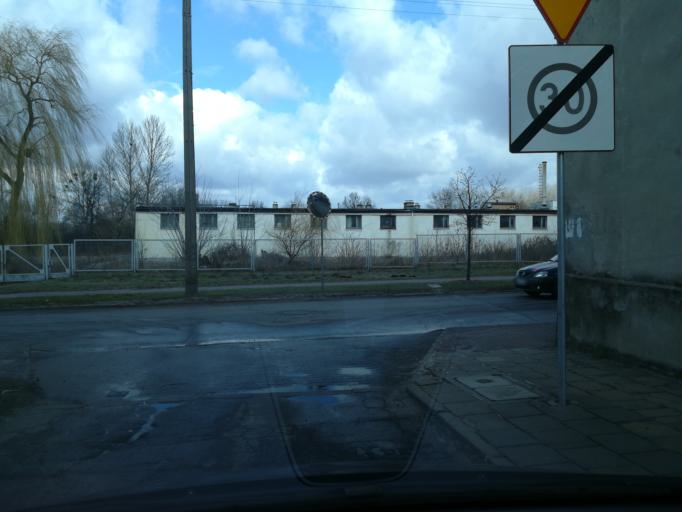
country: PL
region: Silesian Voivodeship
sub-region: Czestochowa
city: Czestochowa
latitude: 50.7938
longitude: 19.1298
